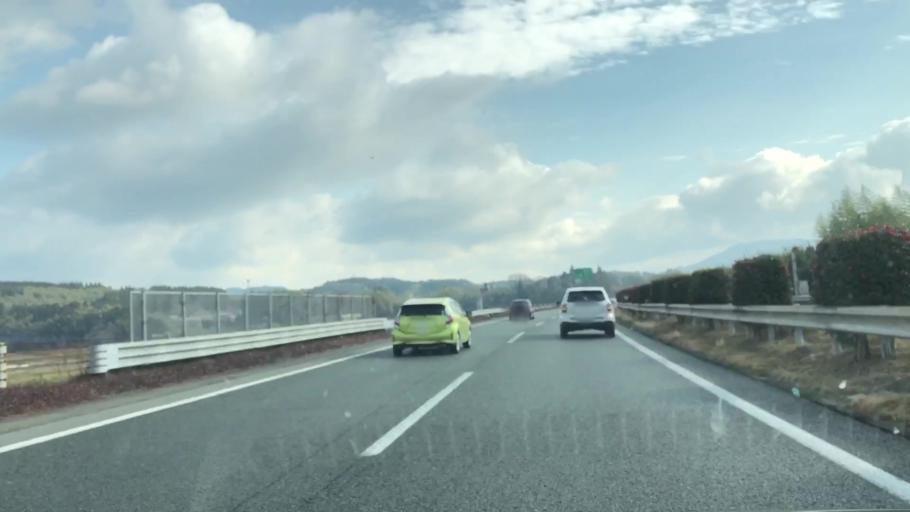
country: JP
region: Kumamoto
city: Tamana
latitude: 32.9945
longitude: 130.5996
